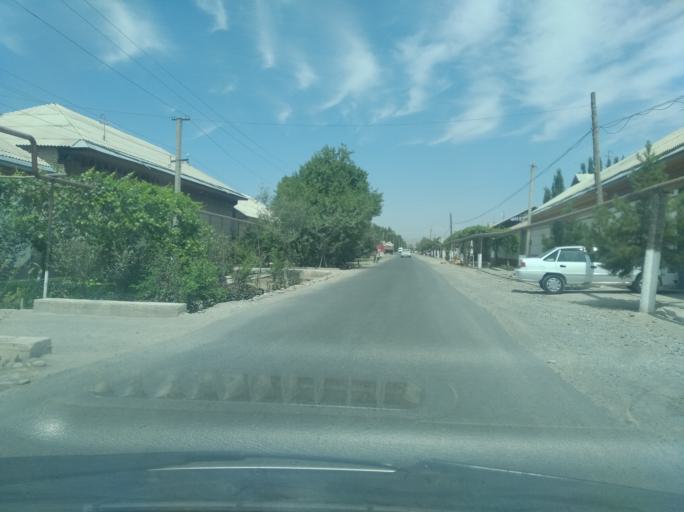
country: KG
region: Osh
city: Aravan
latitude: 40.6094
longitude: 72.4576
